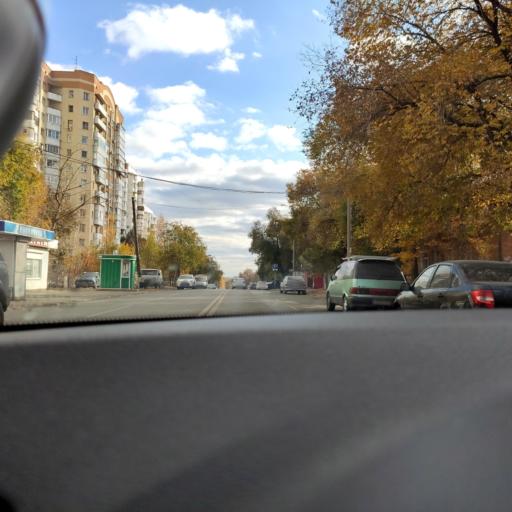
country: RU
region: Samara
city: Samara
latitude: 53.2209
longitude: 50.2308
